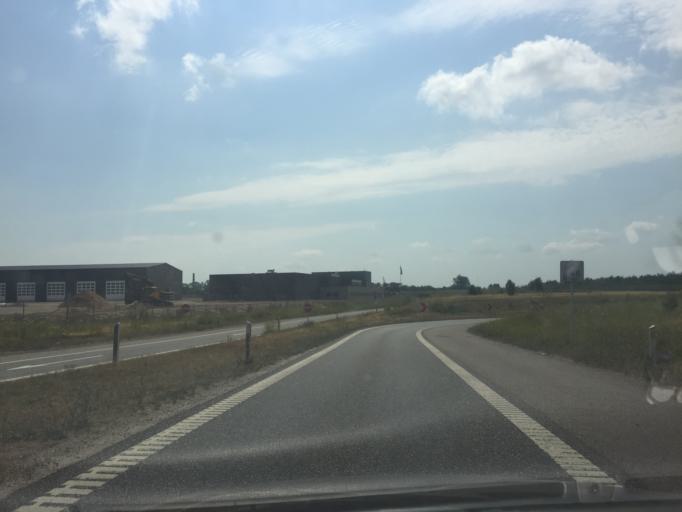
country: DK
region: South Denmark
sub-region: Faaborg-Midtfyn Kommune
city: Ringe
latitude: 55.2565
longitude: 10.4738
